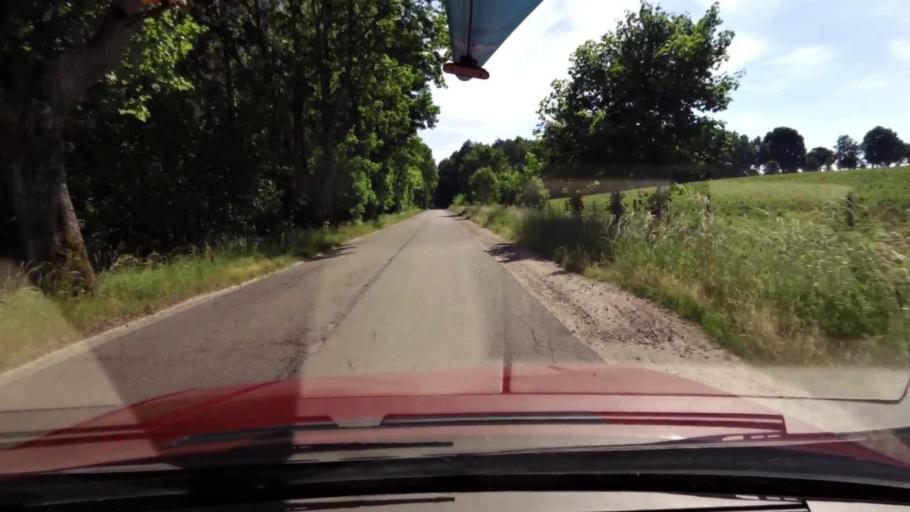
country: PL
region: Pomeranian Voivodeship
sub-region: Powiat slupski
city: Kobylnica
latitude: 54.3392
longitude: 16.9611
